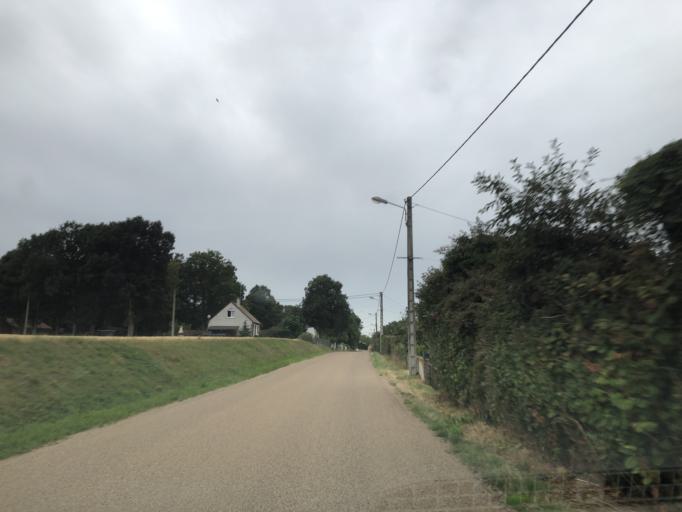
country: FR
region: Bourgogne
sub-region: Departement de l'Yonne
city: Charny
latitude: 47.9449
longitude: 3.1322
